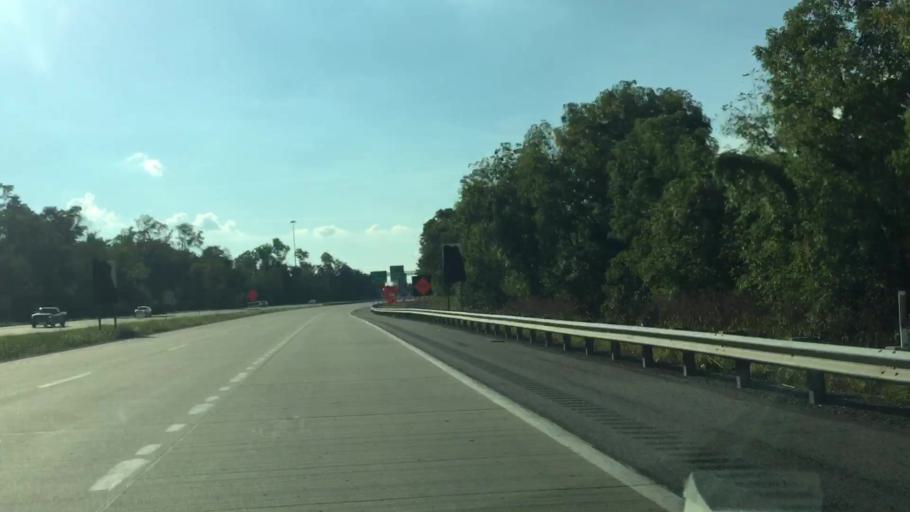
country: US
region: Pennsylvania
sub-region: Allegheny County
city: Carnot-Moon
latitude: 40.5104
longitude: -80.2550
